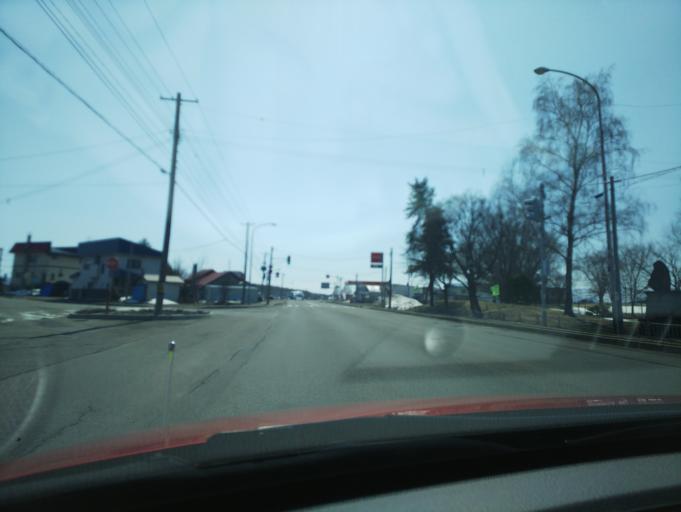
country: JP
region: Hokkaido
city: Nayoro
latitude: 44.2898
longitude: 142.4170
